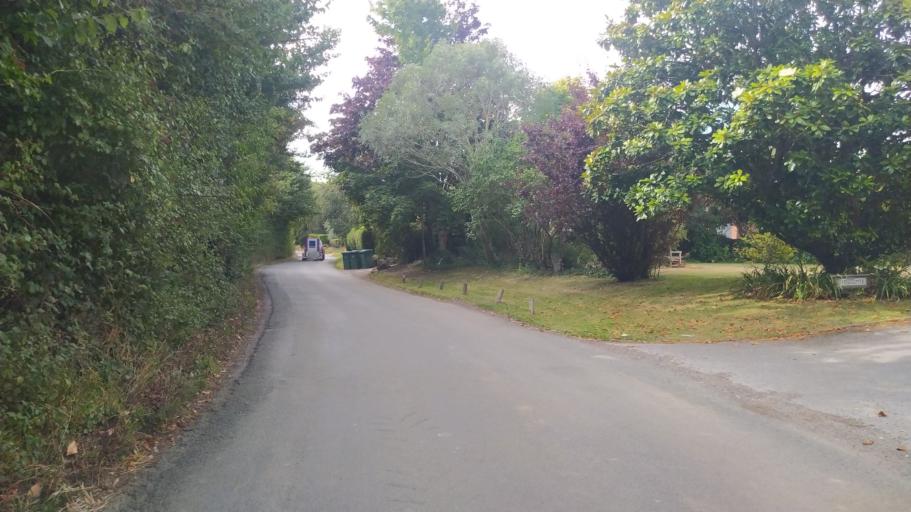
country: GB
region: England
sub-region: West Sussex
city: Chichester
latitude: 50.8093
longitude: -0.7482
